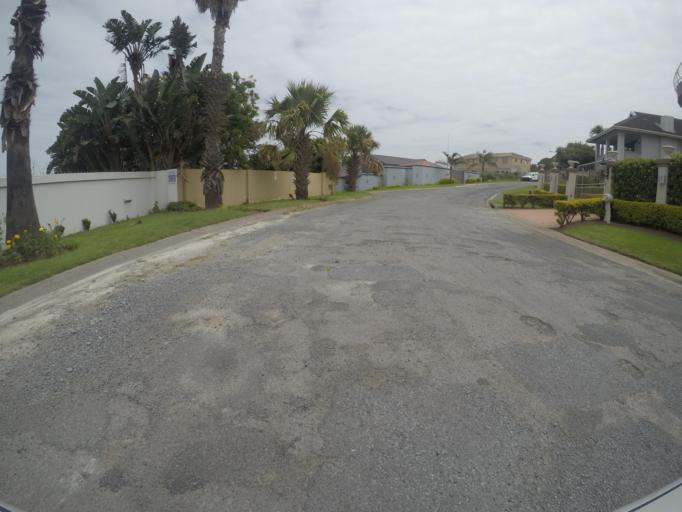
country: ZA
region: Eastern Cape
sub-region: Buffalo City Metropolitan Municipality
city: East London
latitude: -32.9806
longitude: 27.9516
